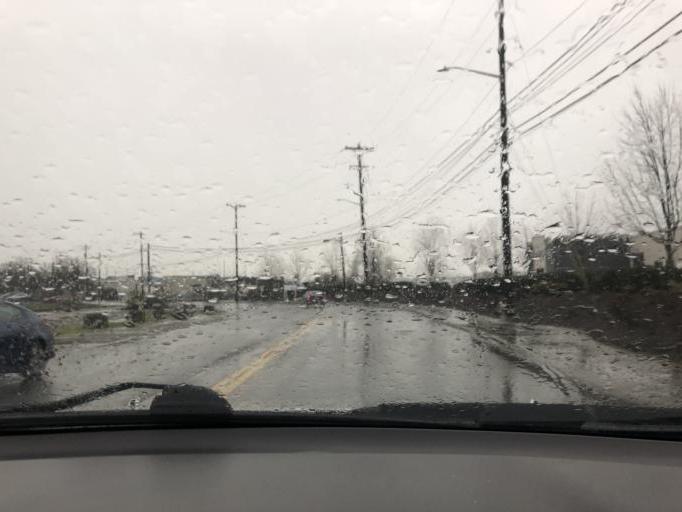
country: US
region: Washington
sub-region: Pierce County
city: Tacoma
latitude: 47.2528
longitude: -122.4238
